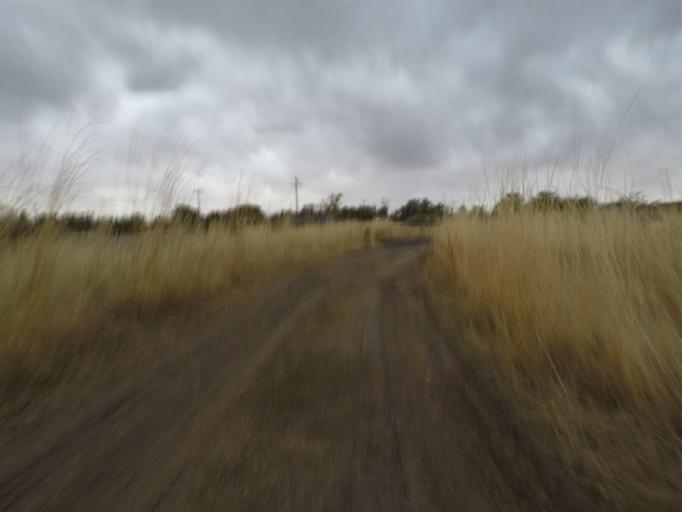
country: US
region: Washington
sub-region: Walla Walla County
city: Walla Walla East
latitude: 46.0744
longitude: -118.2717
